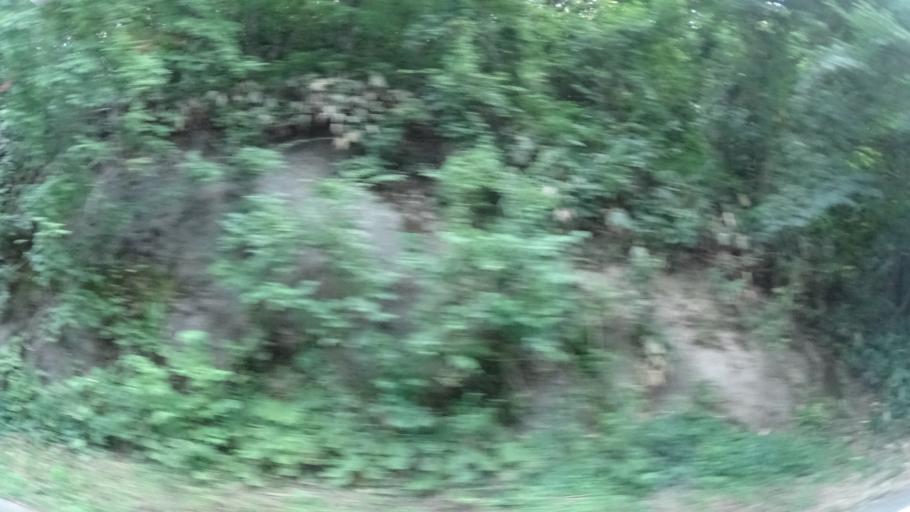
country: JP
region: Ishikawa
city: Nanao
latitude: 37.2729
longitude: 136.8878
